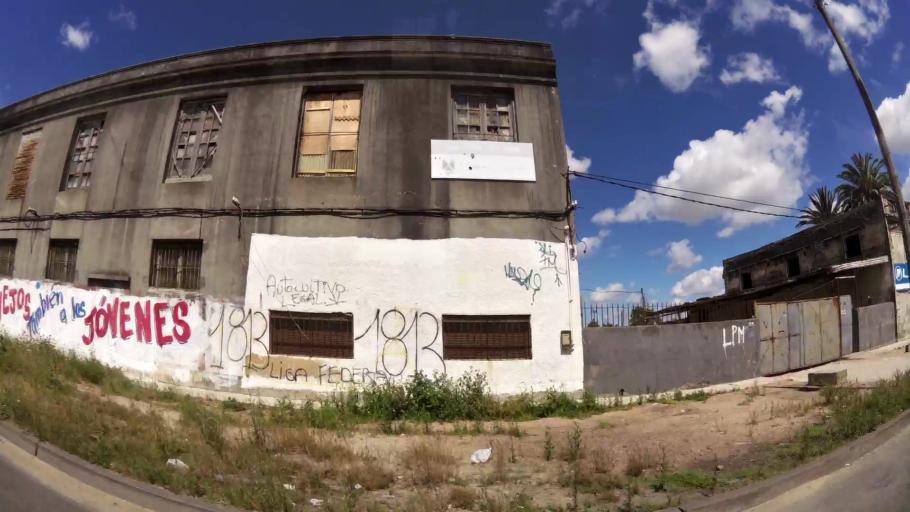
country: UY
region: Montevideo
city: Montevideo
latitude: -34.8427
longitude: -56.1365
